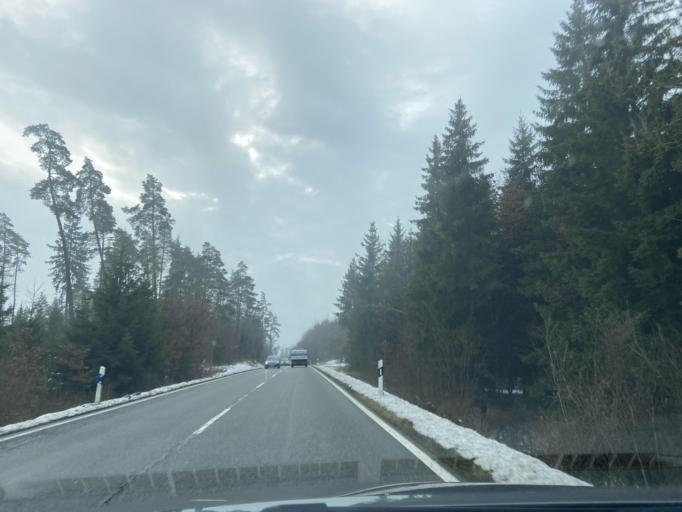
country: DE
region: Baden-Wuerttemberg
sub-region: Tuebingen Region
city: Bingen
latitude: 48.1253
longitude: 9.2643
